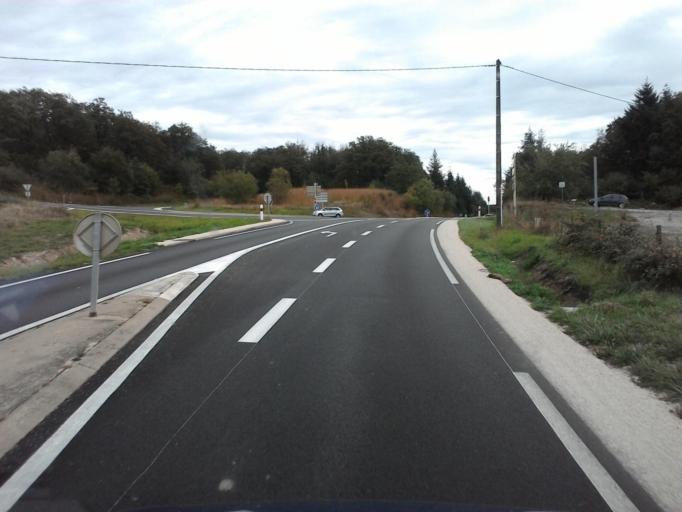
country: FR
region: Bourgogne
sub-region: Departement de Saone-et-Loire
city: Saint-Eusebe
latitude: 46.6190
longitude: 4.4734
